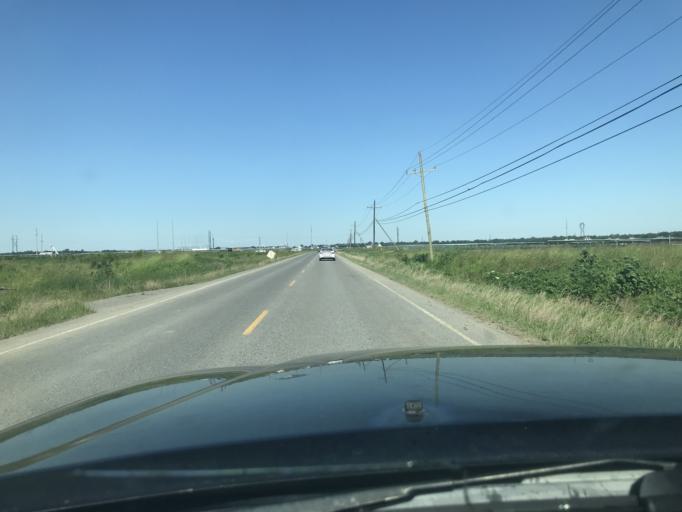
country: US
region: Louisiana
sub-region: West Baton Rouge Parish
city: Brusly
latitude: 30.4688
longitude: -91.3193
